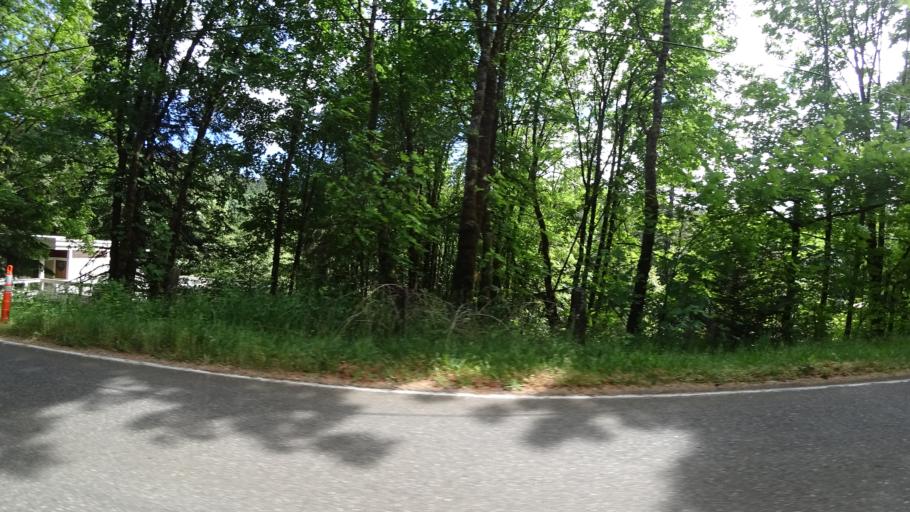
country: US
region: Oregon
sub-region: Washington County
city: Bethany
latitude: 45.6039
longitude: -122.8297
